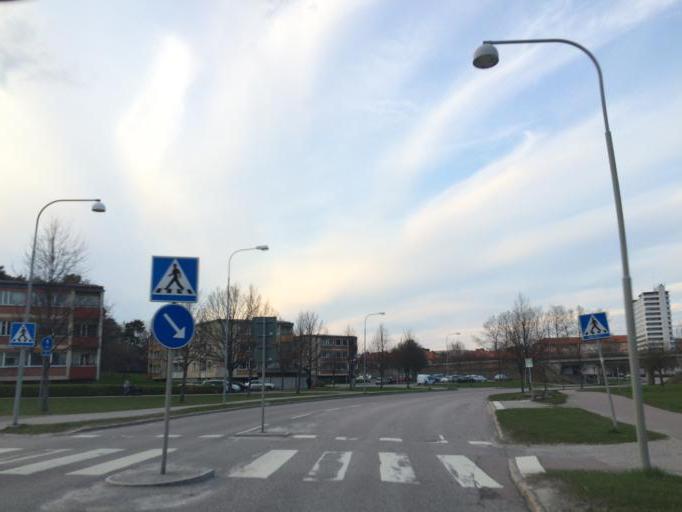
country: SE
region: Soedermanland
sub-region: Eskilstuna Kommun
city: Eskilstuna
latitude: 59.3588
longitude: 16.5310
